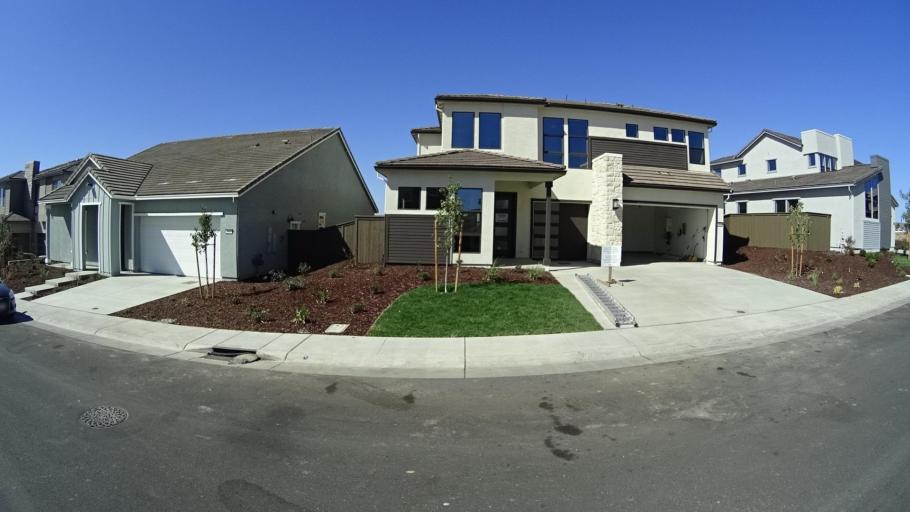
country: US
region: California
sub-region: Placer County
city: Rocklin
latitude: 38.8296
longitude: -121.2614
